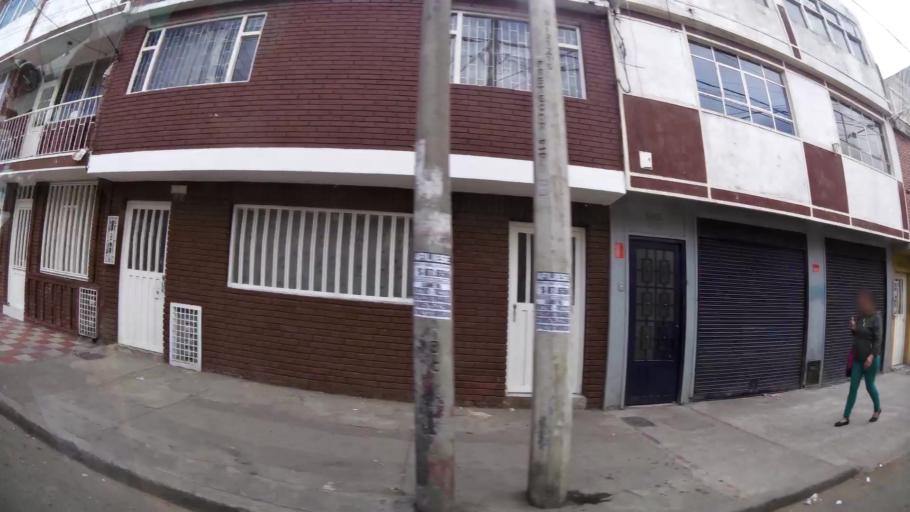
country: CO
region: Bogota D.C.
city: Bogota
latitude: 4.6033
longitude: -74.1272
